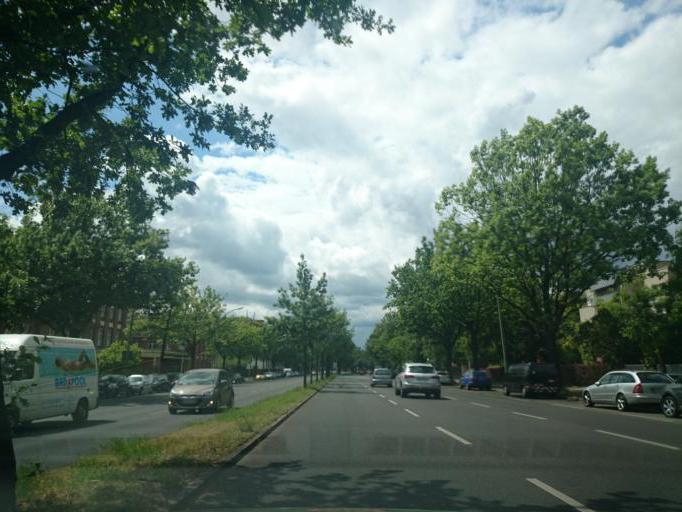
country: DE
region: Berlin
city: Dahlem
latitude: 52.4438
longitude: 13.2885
